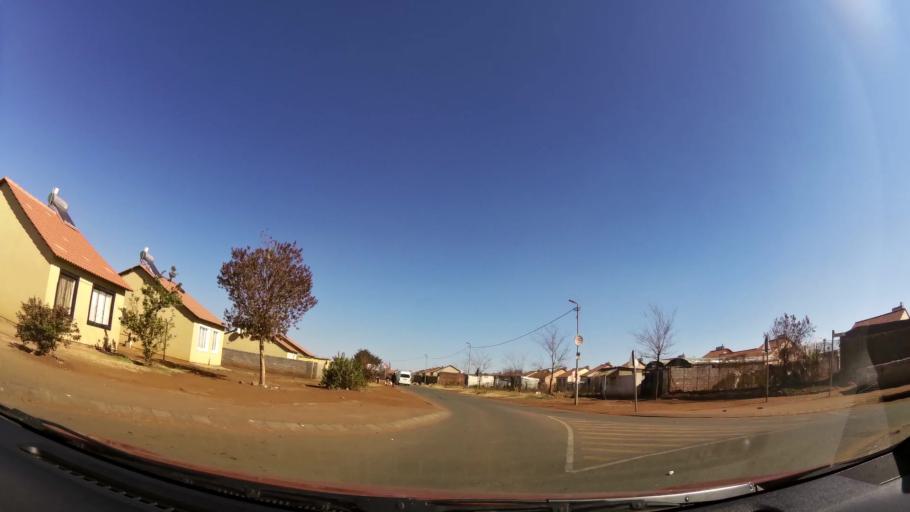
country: ZA
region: Gauteng
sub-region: City of Johannesburg Metropolitan Municipality
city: Soweto
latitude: -26.2370
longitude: 27.8026
